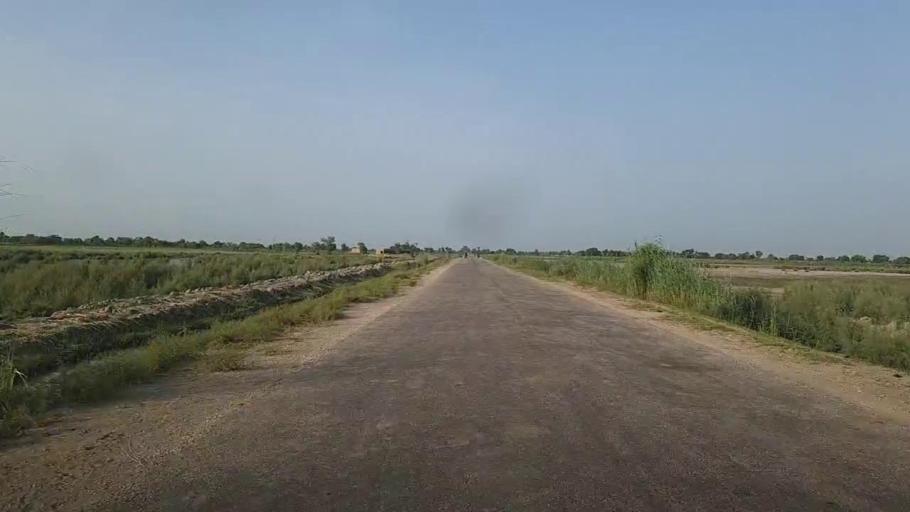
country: PK
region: Sindh
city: Ubauro
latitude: 28.0918
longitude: 69.8048
